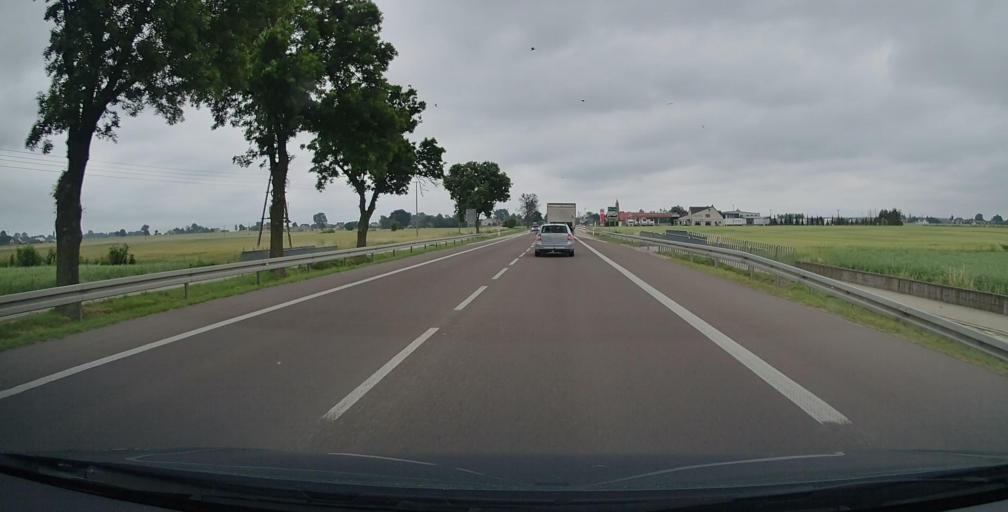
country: PL
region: Lublin Voivodeship
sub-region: Powiat bialski
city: Rzeczyca
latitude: 52.0255
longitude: 22.7148
